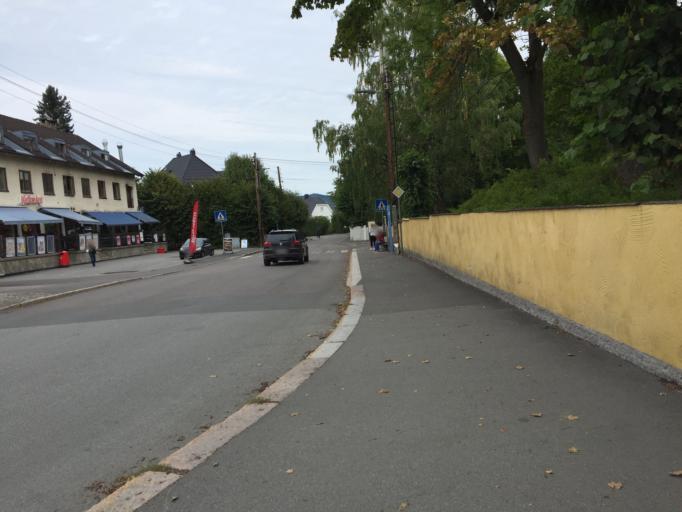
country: NO
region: Oslo
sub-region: Oslo
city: Sjolyststranda
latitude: 59.9029
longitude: 10.6868
